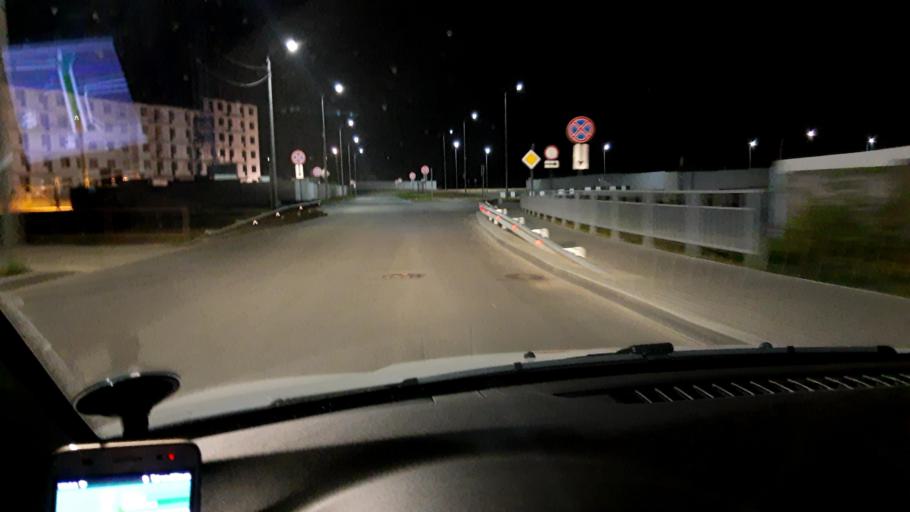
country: RU
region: Nizjnij Novgorod
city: Burevestnik
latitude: 56.2104
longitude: 43.8249
